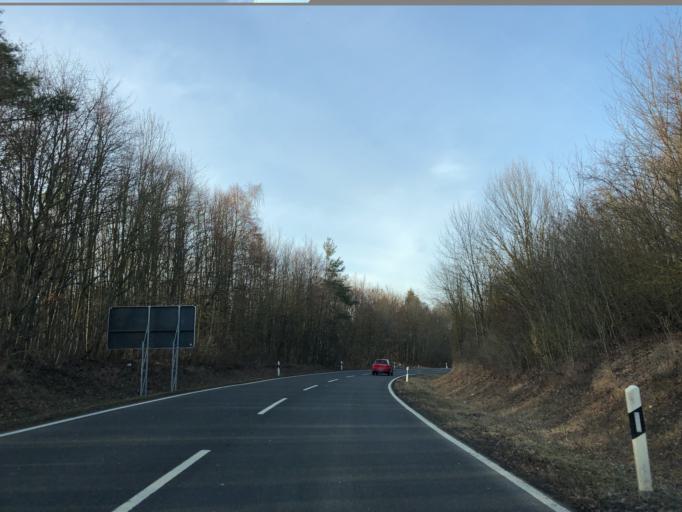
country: DE
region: Bavaria
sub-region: Regierungsbezirk Unterfranken
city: Reichenberg
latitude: 49.7394
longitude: 9.9333
